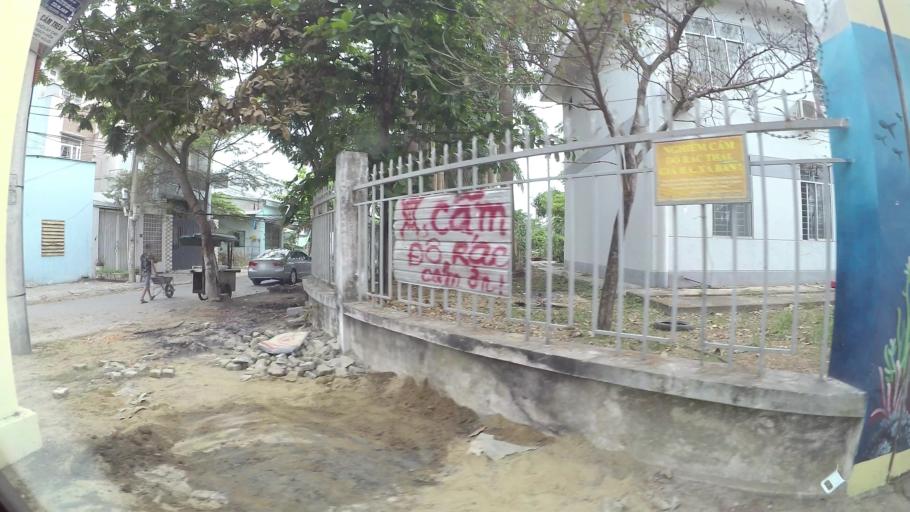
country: VN
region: Da Nang
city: Thanh Khe
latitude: 16.0697
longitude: 108.1942
